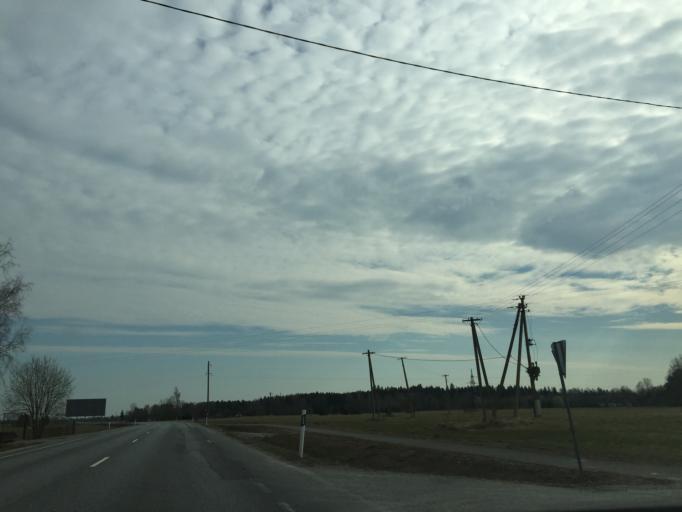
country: EE
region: Ida-Virumaa
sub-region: Johvi vald
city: Johvi
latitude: 59.2920
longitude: 27.4957
